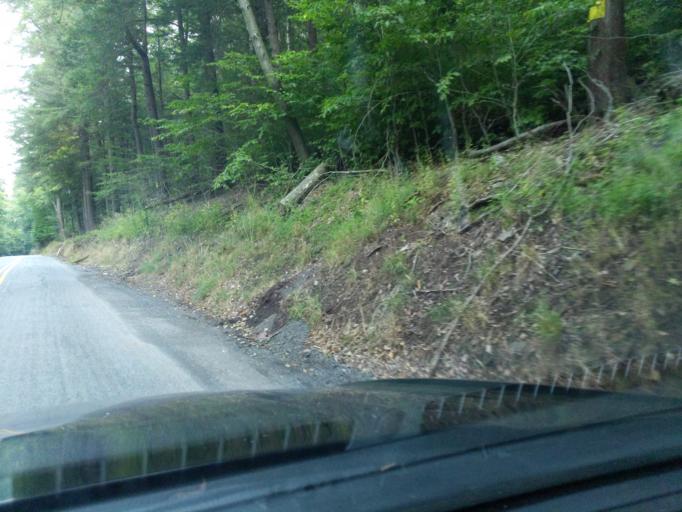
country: US
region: Pennsylvania
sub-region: Cambria County
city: Portage
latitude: 40.3239
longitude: -78.5750
